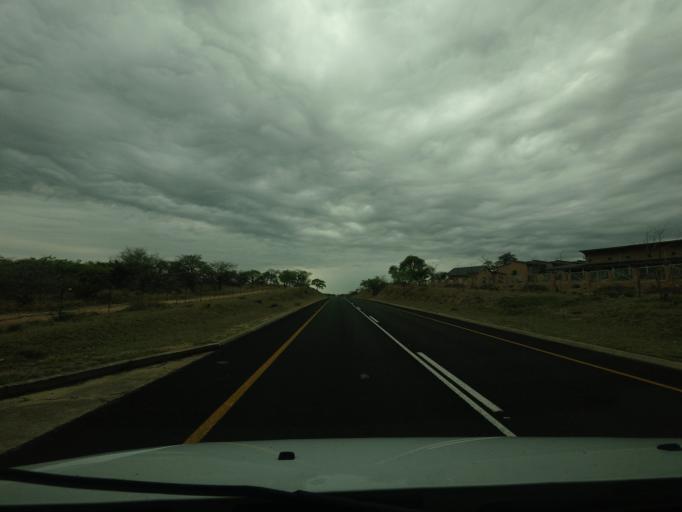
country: ZA
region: Limpopo
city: Thulamahashi
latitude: -24.5680
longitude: 31.0829
